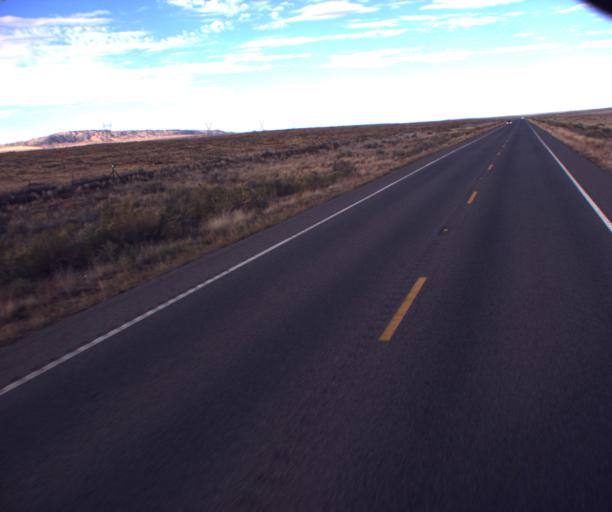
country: US
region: Arizona
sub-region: Apache County
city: Lukachukai
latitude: 36.9414
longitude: -109.2537
